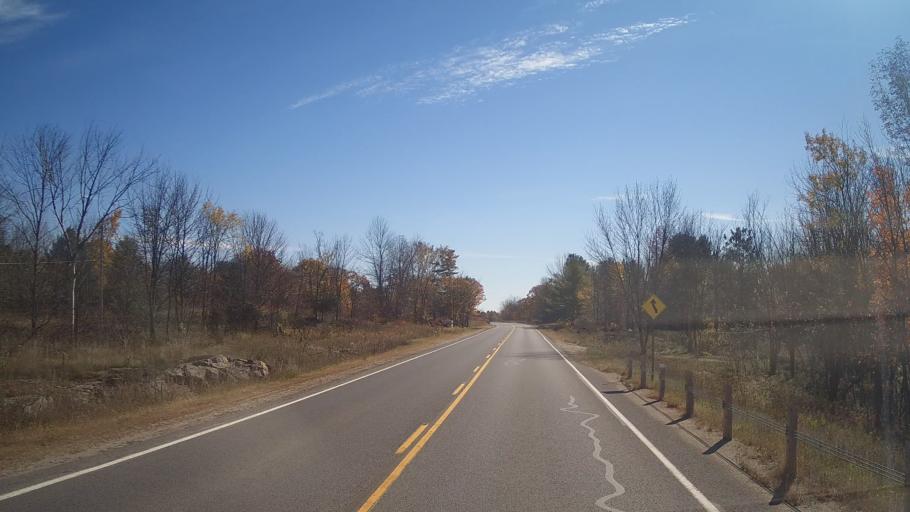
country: CA
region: Ontario
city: Perth
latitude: 44.6870
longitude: -76.6739
